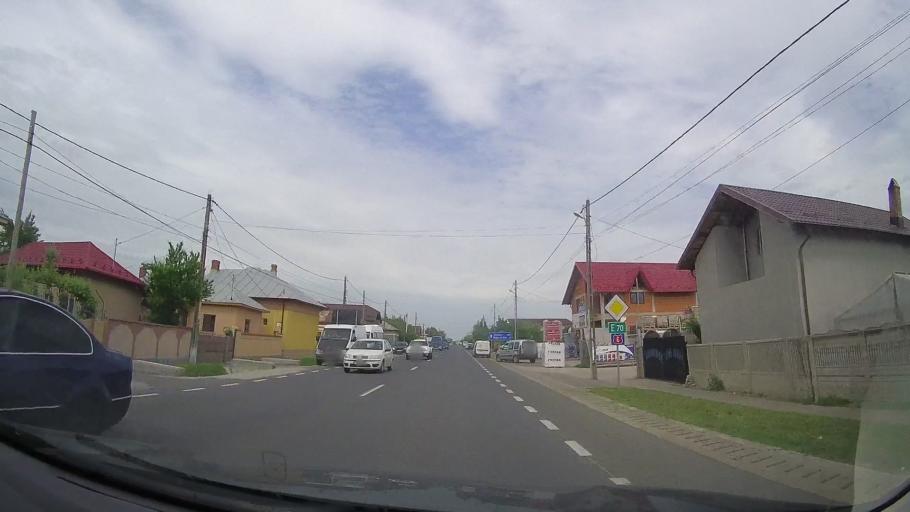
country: RO
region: Teleorman
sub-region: Comuna Peretu
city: Peretu
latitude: 44.0433
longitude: 25.0890
